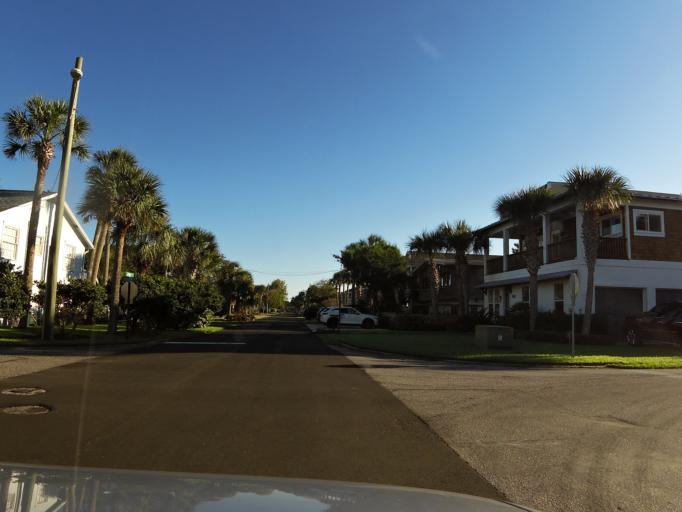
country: US
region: Florida
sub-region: Duval County
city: Neptune Beach
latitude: 30.3194
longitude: -81.3966
